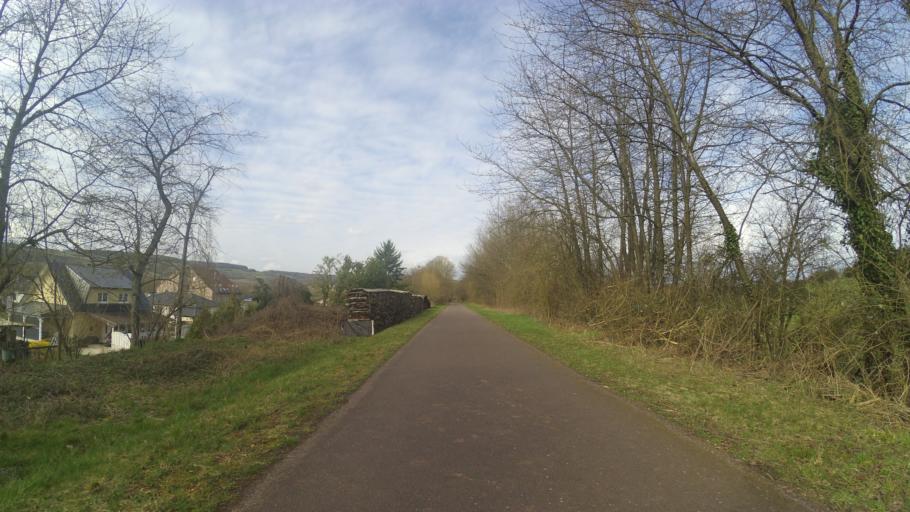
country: FR
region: Lorraine
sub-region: Departement de la Moselle
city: Bliesbruck
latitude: 49.1231
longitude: 7.1851
